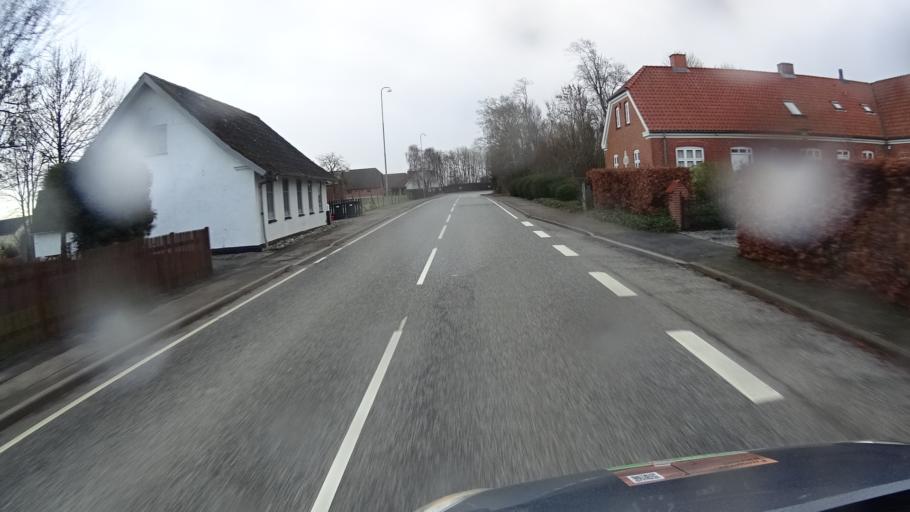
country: DK
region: South Denmark
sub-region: Vejle Kommune
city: Jelling
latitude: 55.7606
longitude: 9.4672
